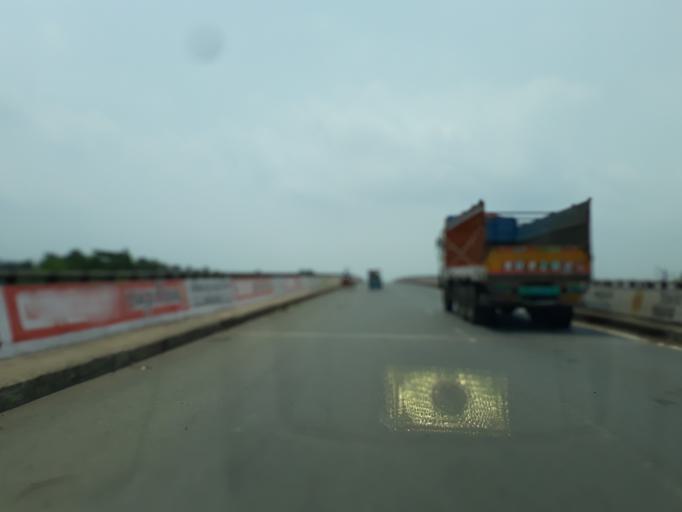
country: IN
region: West Bengal
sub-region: Purba Medinipur
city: Mahishadal
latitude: 22.1867
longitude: 87.9215
